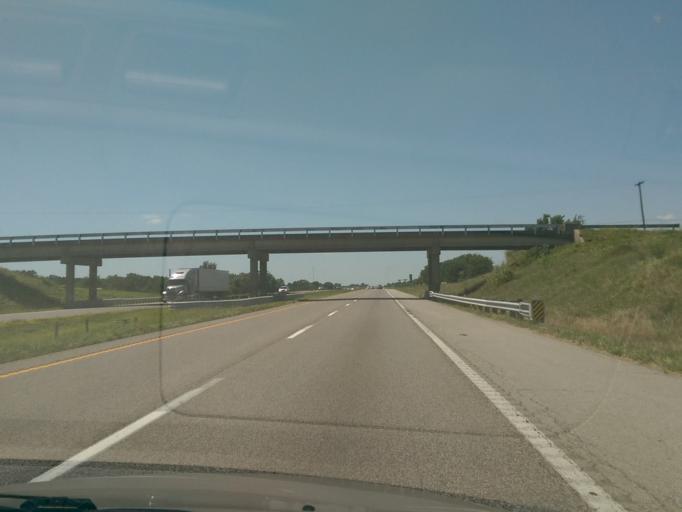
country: US
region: Missouri
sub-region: Saline County
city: Marshall
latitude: 38.9518
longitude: -93.0676
